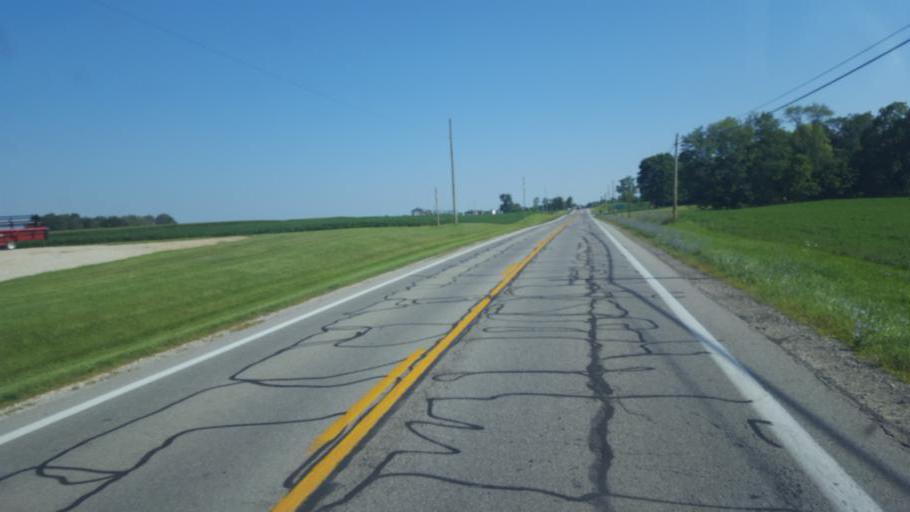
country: US
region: Ohio
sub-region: Morrow County
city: Mount Gilead
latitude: 40.5943
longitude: -82.8237
